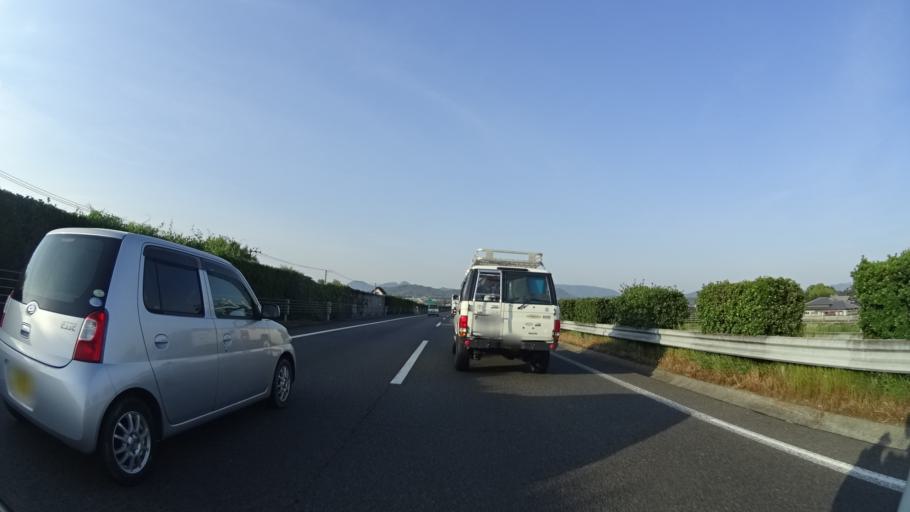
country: JP
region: Kagawa
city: Kan'onjicho
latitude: 34.1210
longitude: 133.6914
